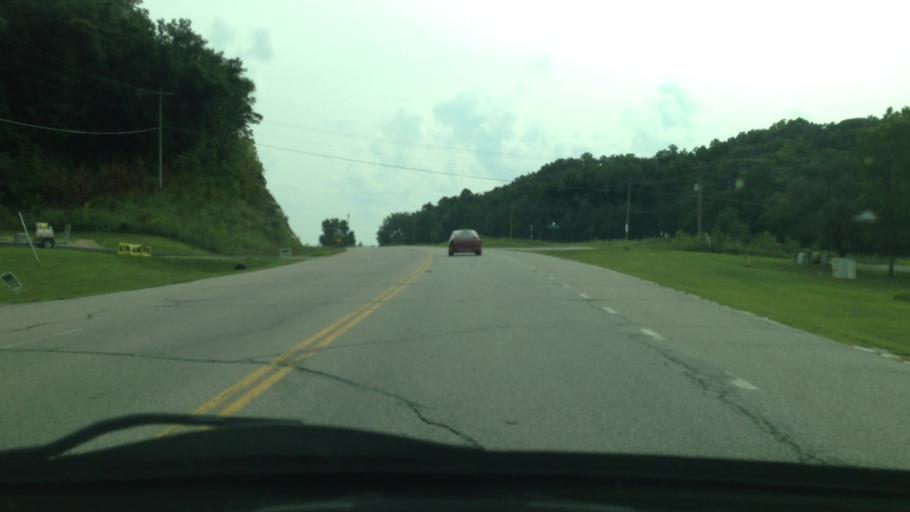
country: US
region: Minnesota
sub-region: Olmsted County
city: Rochester
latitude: 44.0800
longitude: -92.4494
